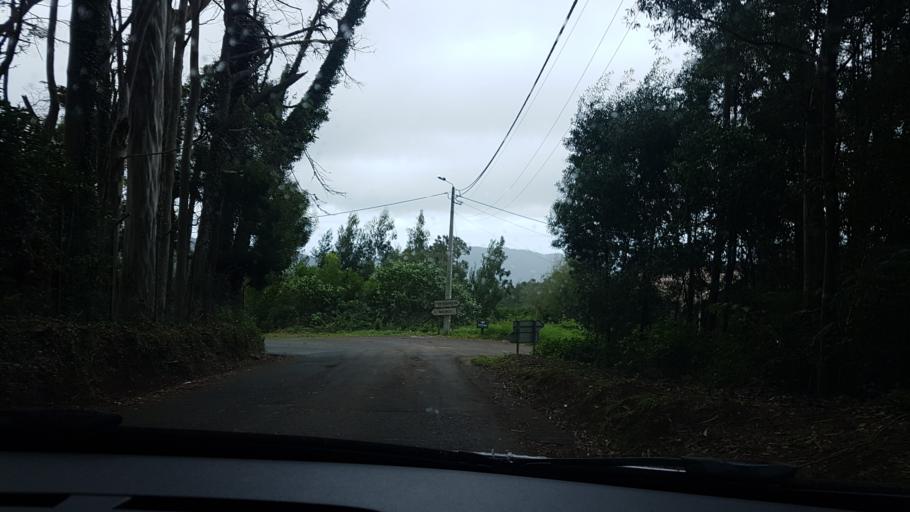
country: PT
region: Madeira
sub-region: Santa Cruz
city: Santa Cruz
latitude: 32.7261
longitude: -16.8153
